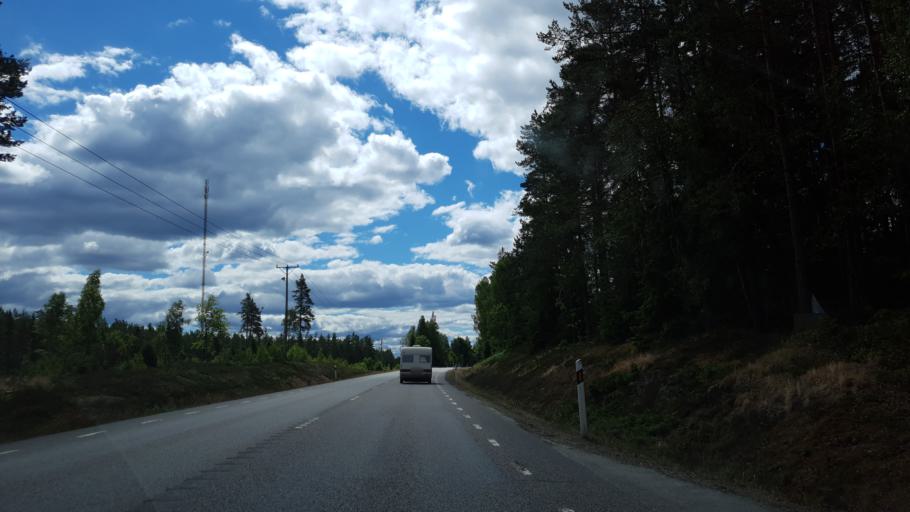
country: SE
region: Kronoberg
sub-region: Vaxjo Kommun
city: Braas
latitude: 57.1357
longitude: 15.1714
